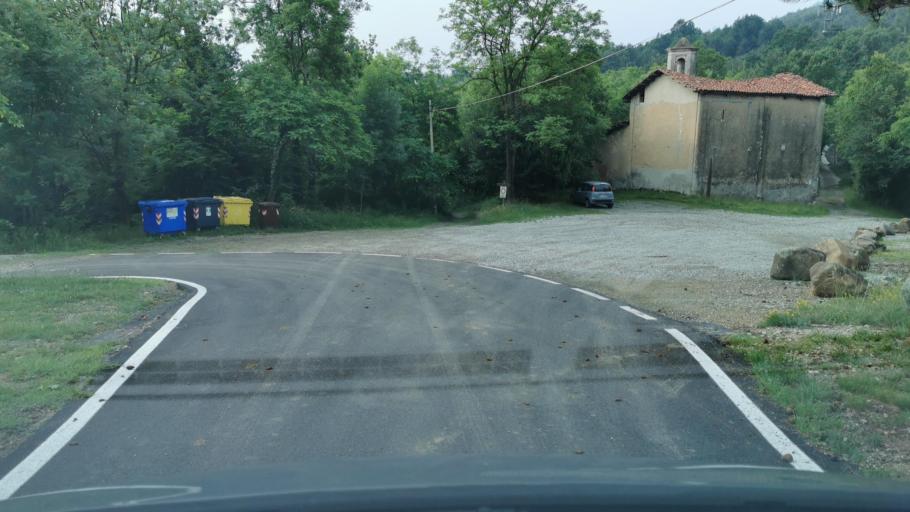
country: IT
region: Piedmont
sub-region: Provincia di Torino
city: Vallo Torinese
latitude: 45.2107
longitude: 7.5003
